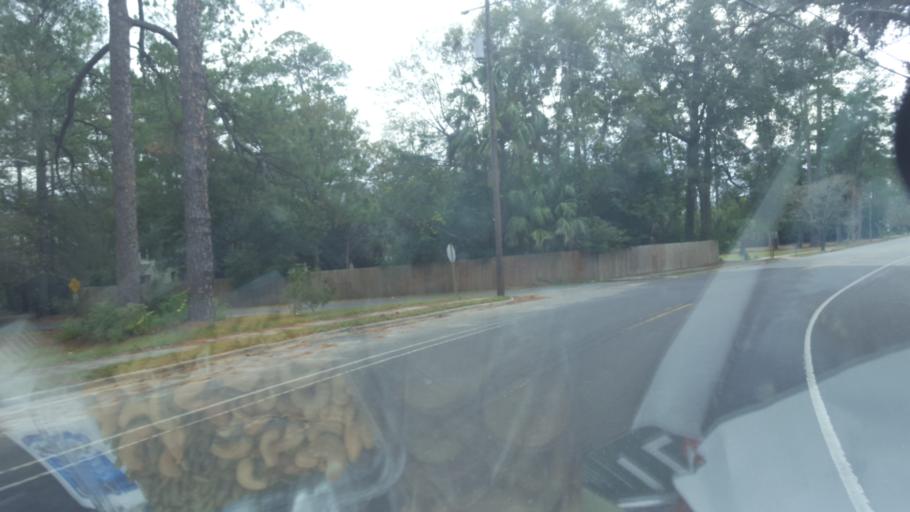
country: US
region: Georgia
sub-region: Berrien County
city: Nashville
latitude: 31.2029
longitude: -83.2550
